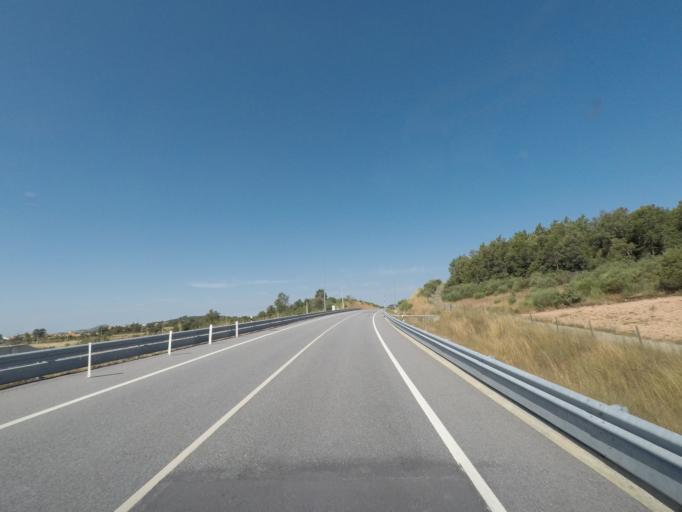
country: PT
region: Braganca
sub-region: Mogadouro
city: Mogadouro
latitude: 41.3450
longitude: -6.6300
